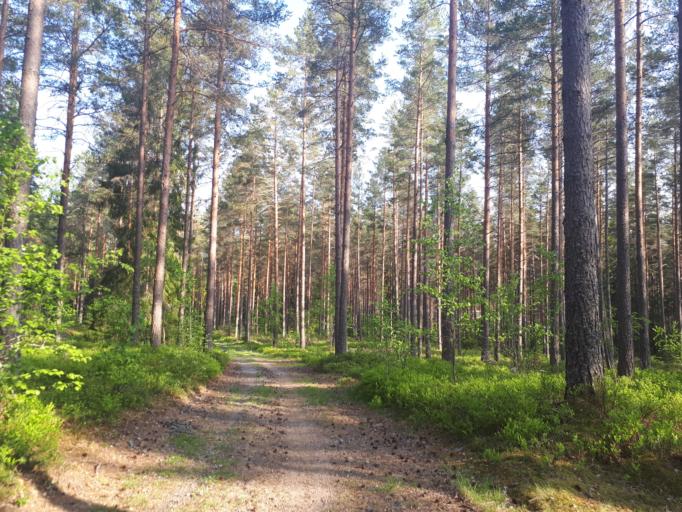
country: SE
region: Soedermanland
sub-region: Flens Kommun
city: Halleforsnas
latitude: 59.0658
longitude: 16.3971
